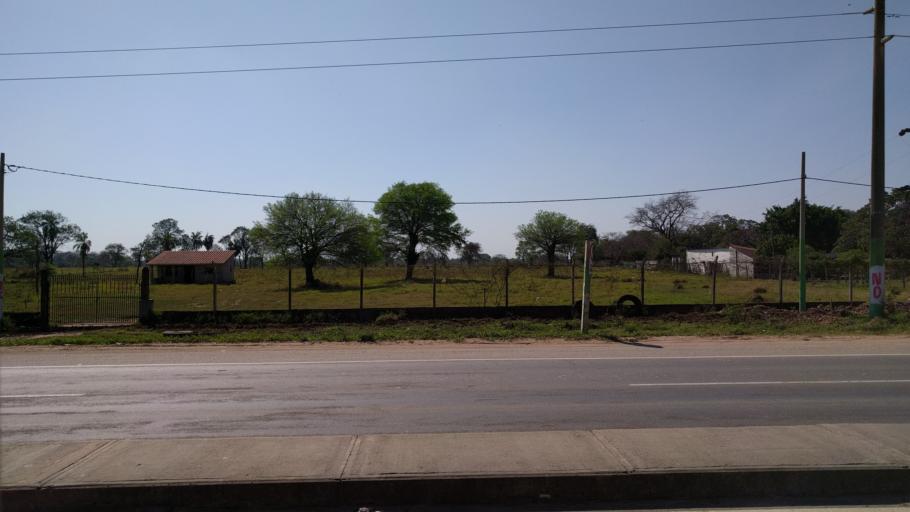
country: BO
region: Santa Cruz
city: Cotoca
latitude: -17.7617
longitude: -63.0230
